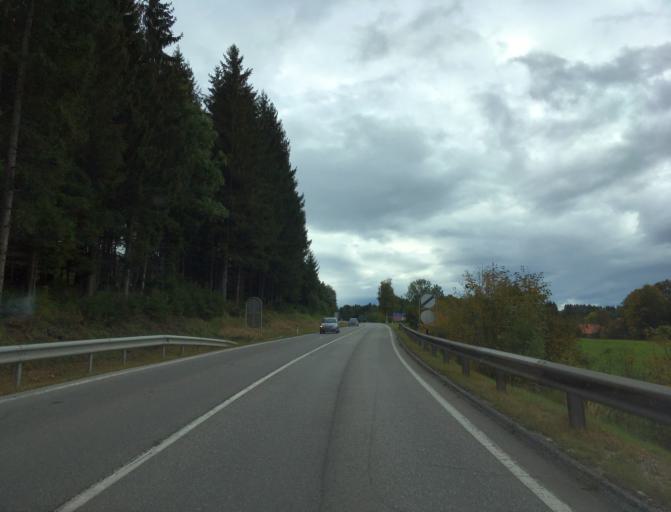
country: AT
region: Lower Austria
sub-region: Politischer Bezirk Neunkirchen
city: Thomasberg
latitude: 47.5461
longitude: 16.1473
